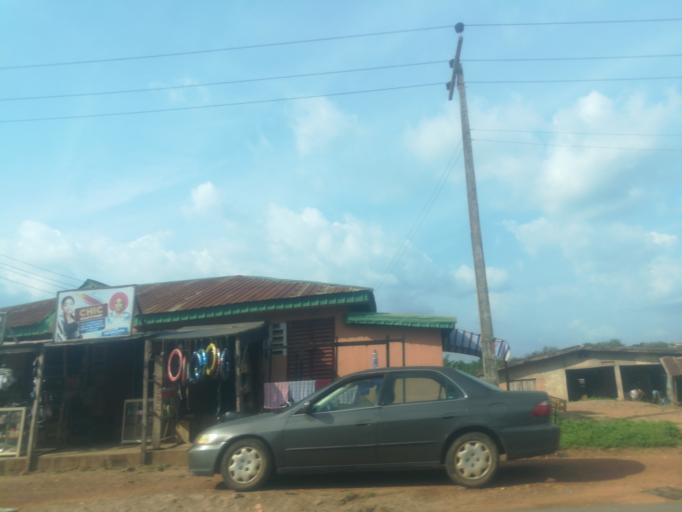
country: NG
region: Oyo
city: Ido
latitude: 7.3960
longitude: 3.7883
